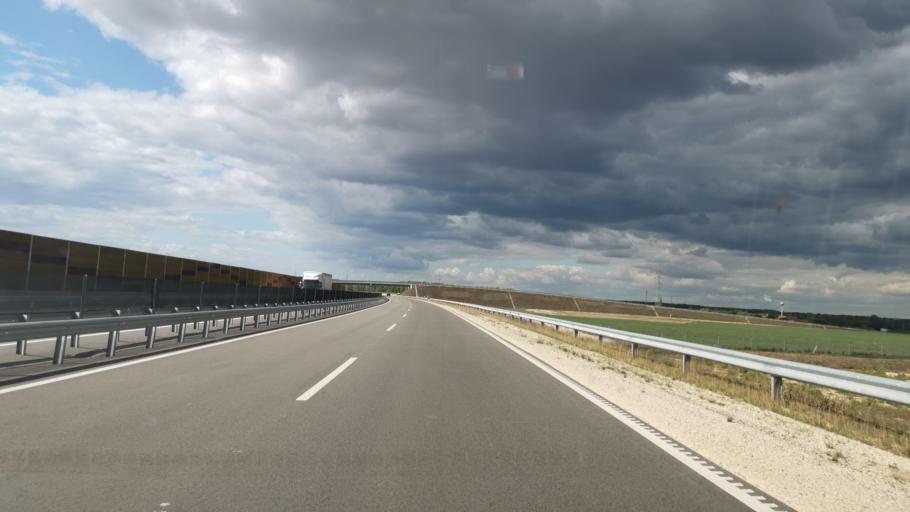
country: HU
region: Jasz-Nagykun-Szolnok
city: Tiszapuspoki
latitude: 47.2010
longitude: 20.3270
